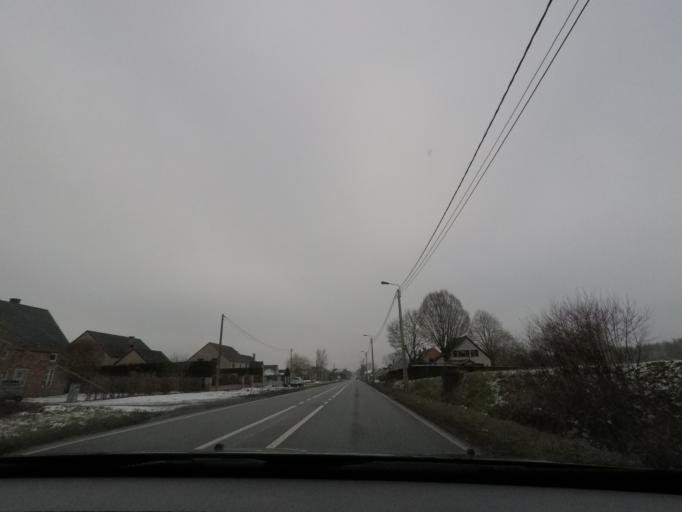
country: BE
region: Wallonia
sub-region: Province de Namur
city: Fosses-la-Ville
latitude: 50.4775
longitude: 4.6729
